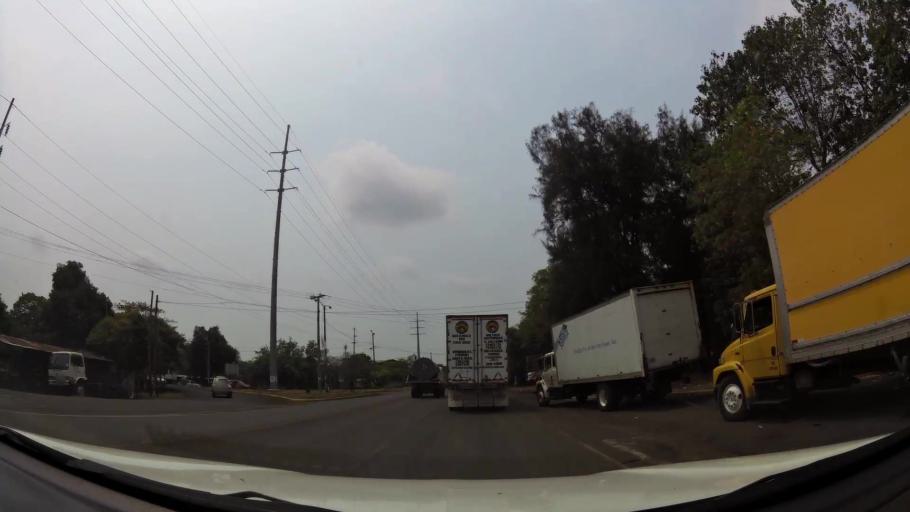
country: NI
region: Chinandega
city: Chinandega
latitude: 12.6408
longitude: -87.1284
